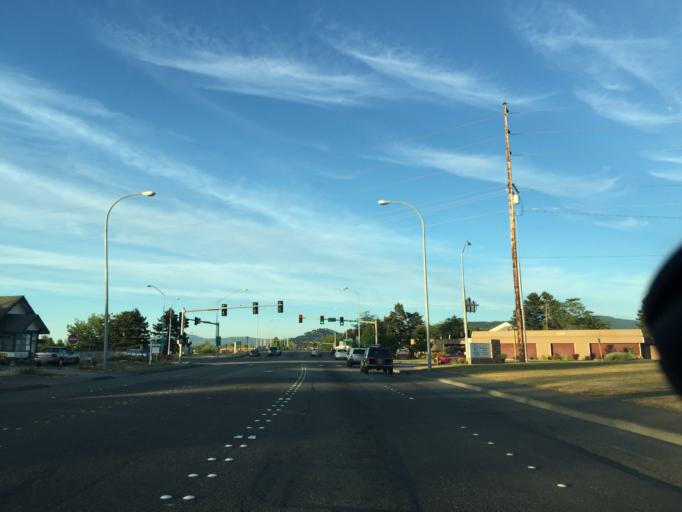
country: US
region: Washington
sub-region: Whatcom County
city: Bellingham
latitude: 48.7701
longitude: -122.4659
